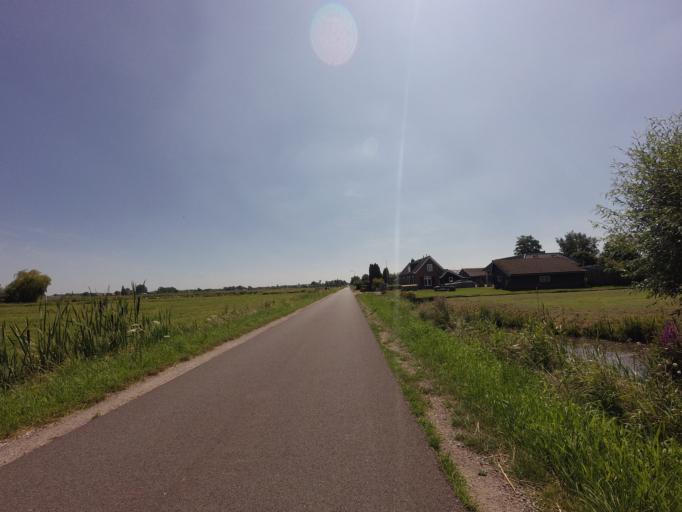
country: NL
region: Utrecht
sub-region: Stichtse Vecht
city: Maarssen
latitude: 52.1661
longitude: 5.0631
